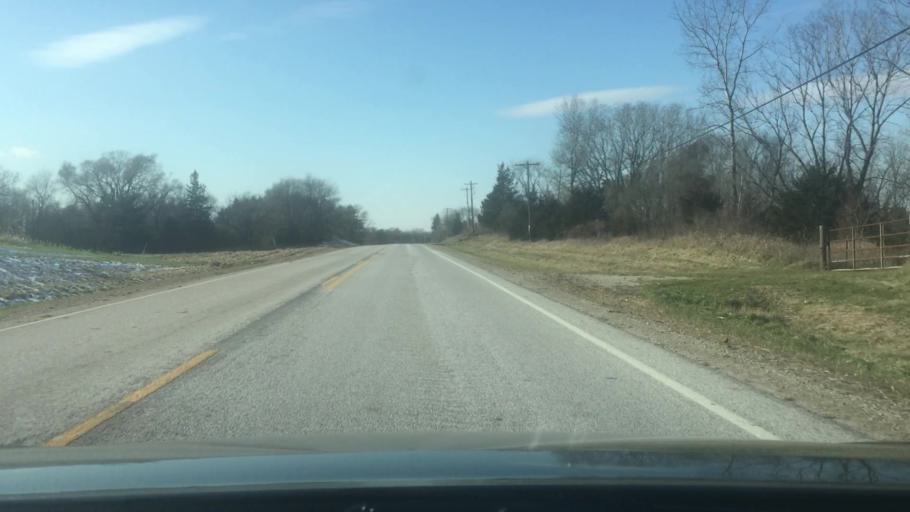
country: US
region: Wisconsin
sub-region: Jefferson County
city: Lake Koshkonong
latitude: 42.9482
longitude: -88.8976
